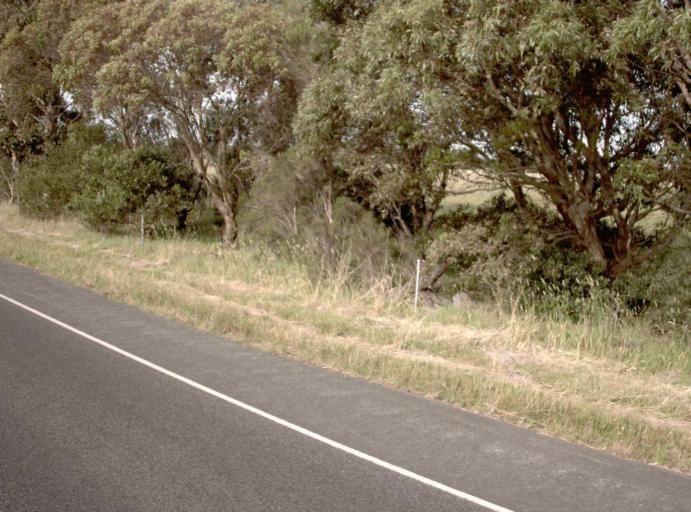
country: AU
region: Victoria
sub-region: Latrobe
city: Traralgon
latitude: -38.1363
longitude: 146.5576
